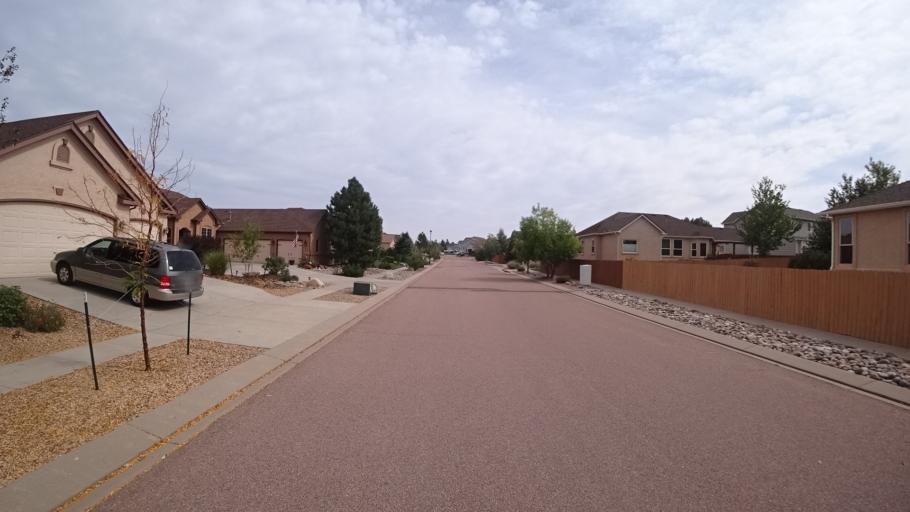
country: US
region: Colorado
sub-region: El Paso County
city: Cimarron Hills
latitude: 38.9167
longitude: -104.6968
